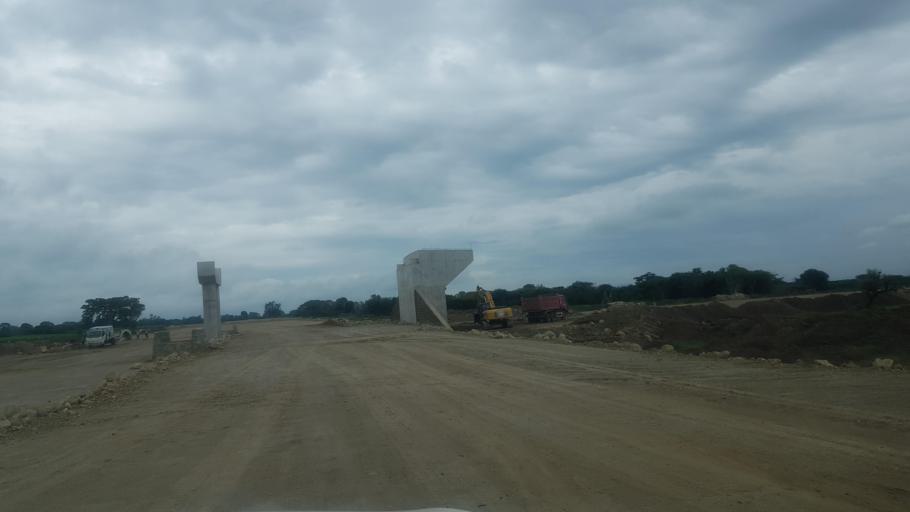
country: ET
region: Oromiya
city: Shashemene
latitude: 7.3552
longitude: 38.6396
